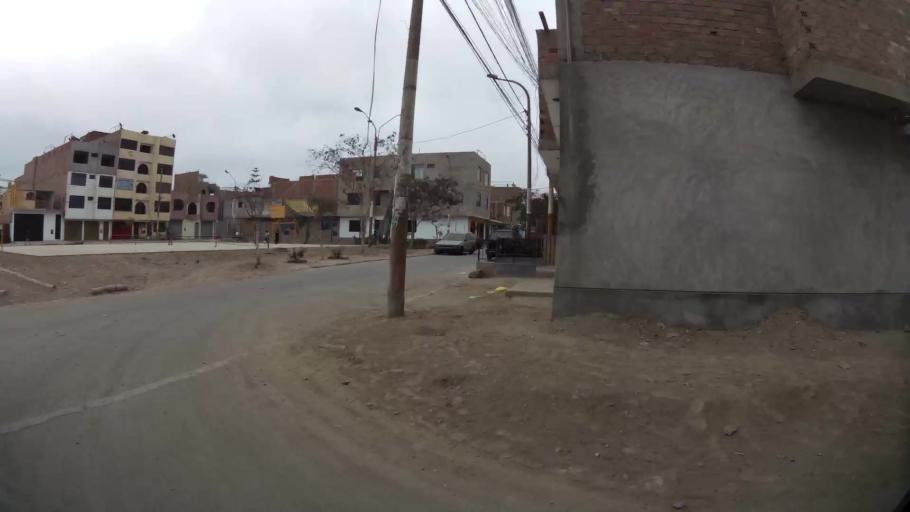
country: PE
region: Lima
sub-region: Lima
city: Independencia
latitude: -11.9683
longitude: -77.0910
